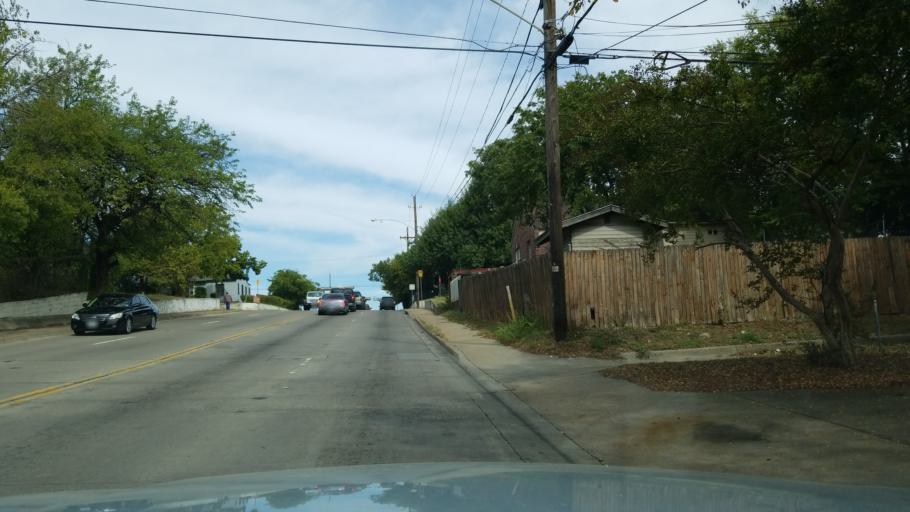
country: US
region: Texas
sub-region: Dallas County
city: Dallas
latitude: 32.7897
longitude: -96.7374
